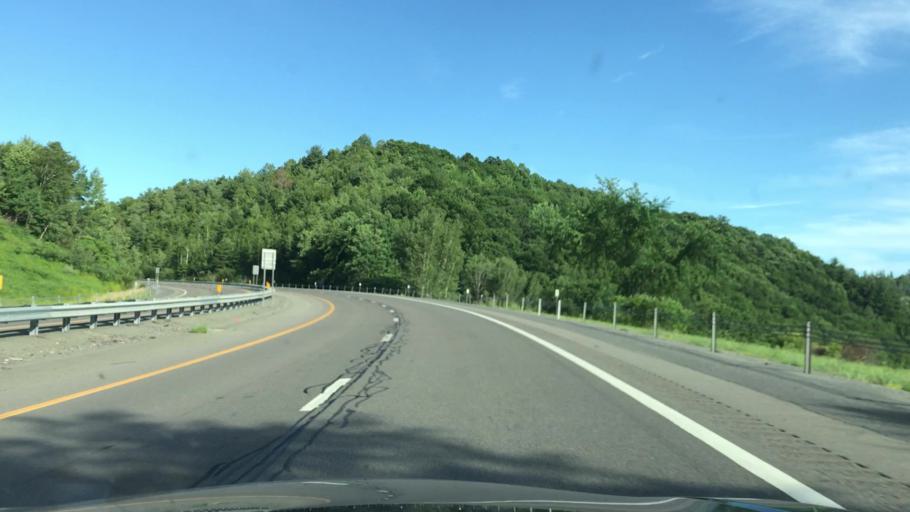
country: US
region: New York
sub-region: Delaware County
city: Hancock
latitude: 41.9569
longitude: -75.2437
